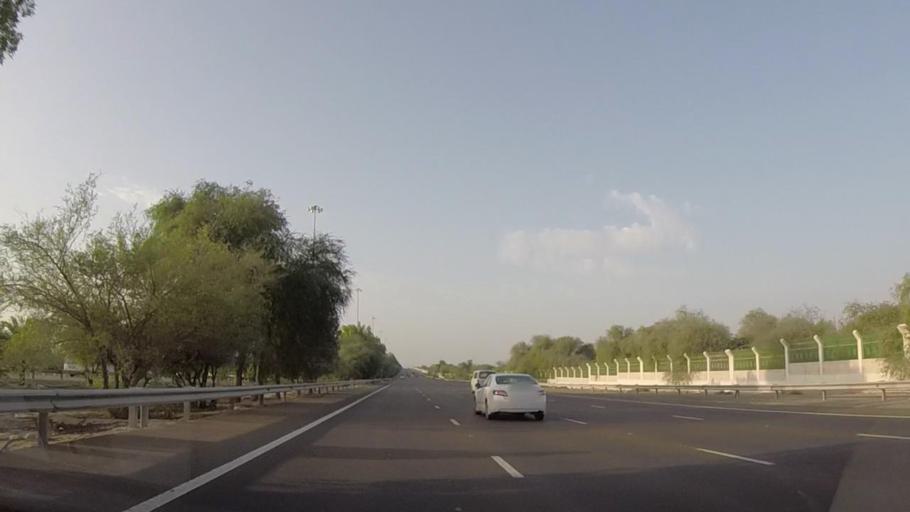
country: AE
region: Dubai
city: Dubai
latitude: 24.7655
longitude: 54.8460
